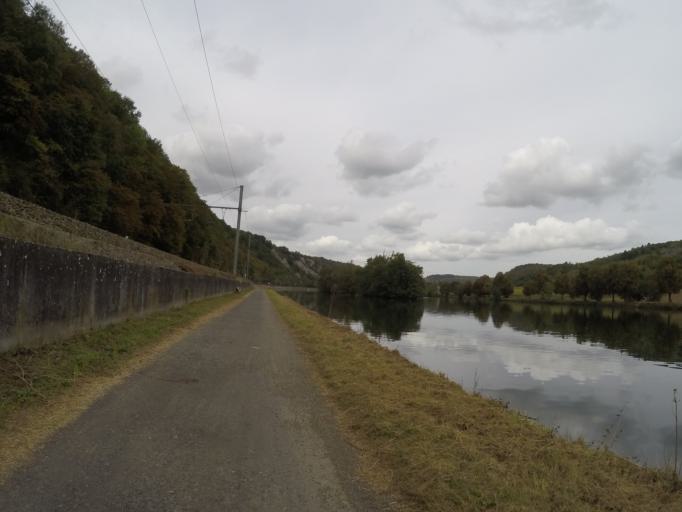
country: BE
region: Wallonia
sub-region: Province de Namur
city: Dinant
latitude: 50.2803
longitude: 4.8930
